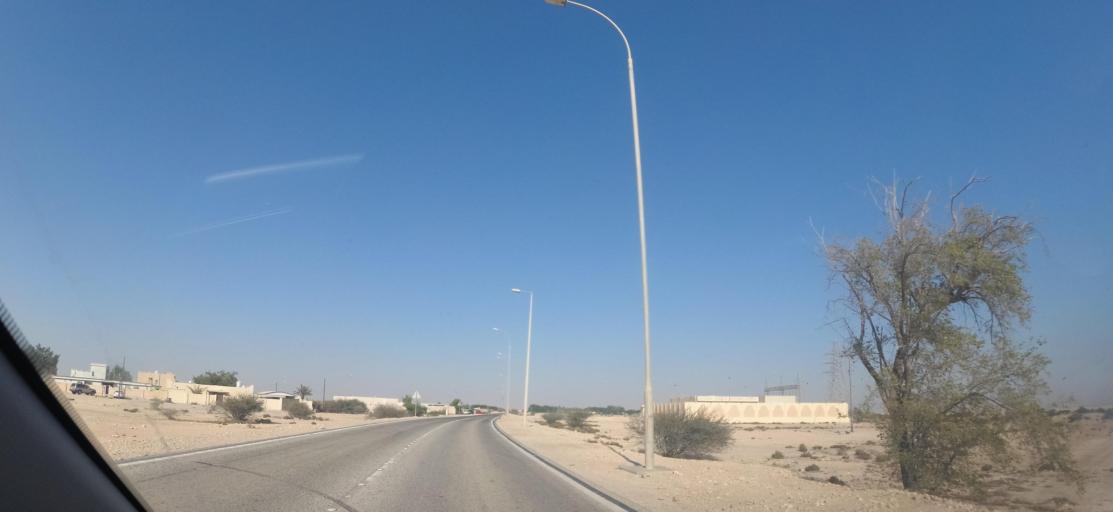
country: QA
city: Al Jumayliyah
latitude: 25.6196
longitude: 51.0858
